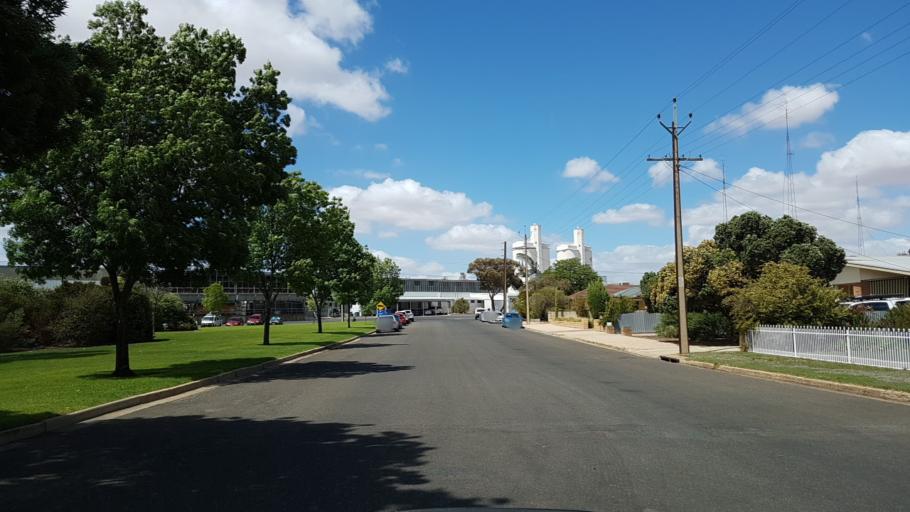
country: AU
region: South Australia
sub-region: Loxton Waikerie
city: Waikerie
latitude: -34.1826
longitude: 139.9876
